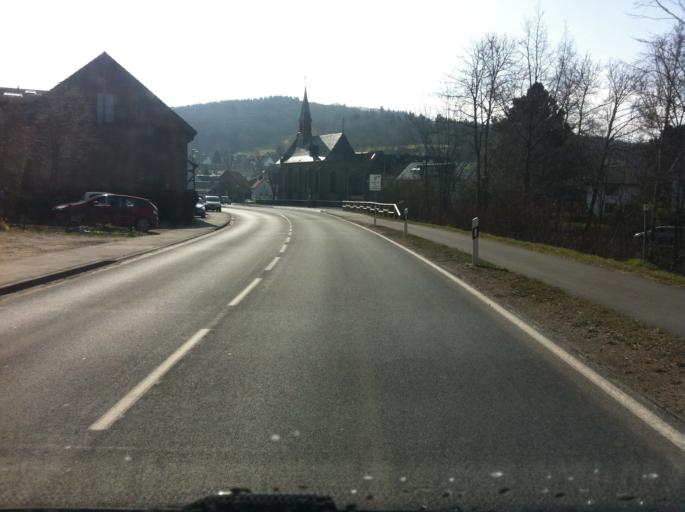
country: DE
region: North Rhine-Westphalia
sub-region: Regierungsbezirk Koln
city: Bad Munstereifel
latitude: 50.5347
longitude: 6.7696
